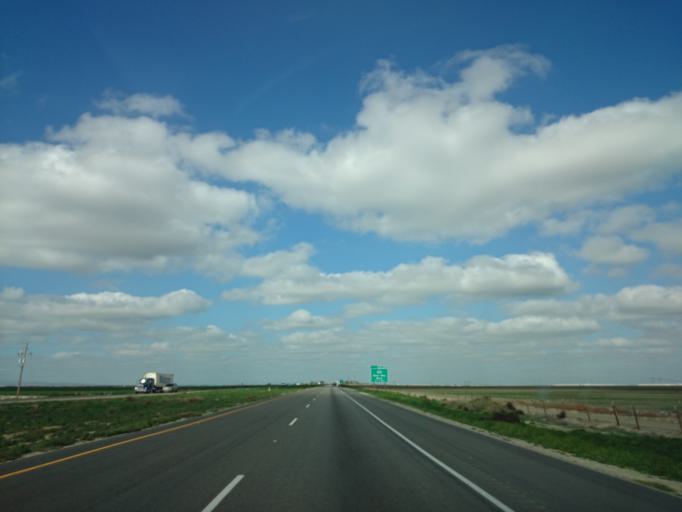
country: US
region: California
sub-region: Kern County
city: Greenfield
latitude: 35.1946
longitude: -119.1470
